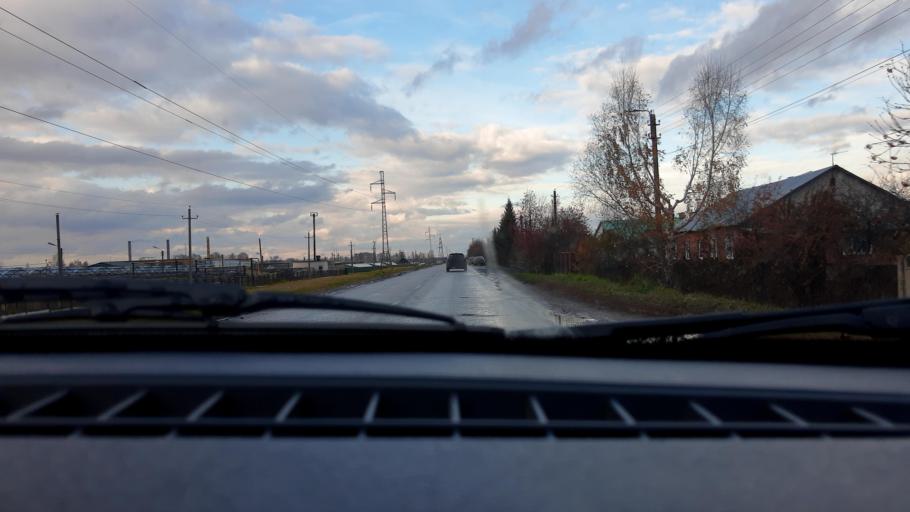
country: RU
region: Bashkortostan
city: Ufa
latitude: 54.8379
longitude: 55.9974
